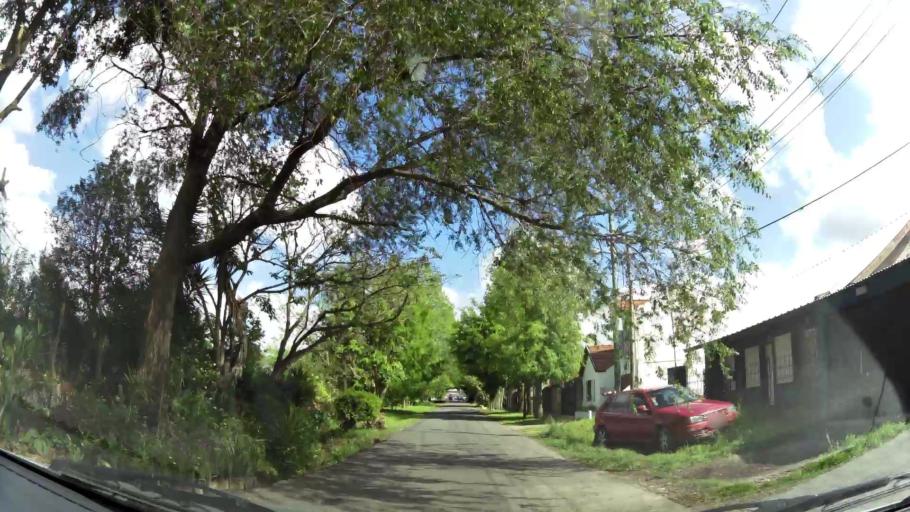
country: AR
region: Buenos Aires
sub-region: Partido de Quilmes
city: Quilmes
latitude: -34.7993
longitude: -58.1597
